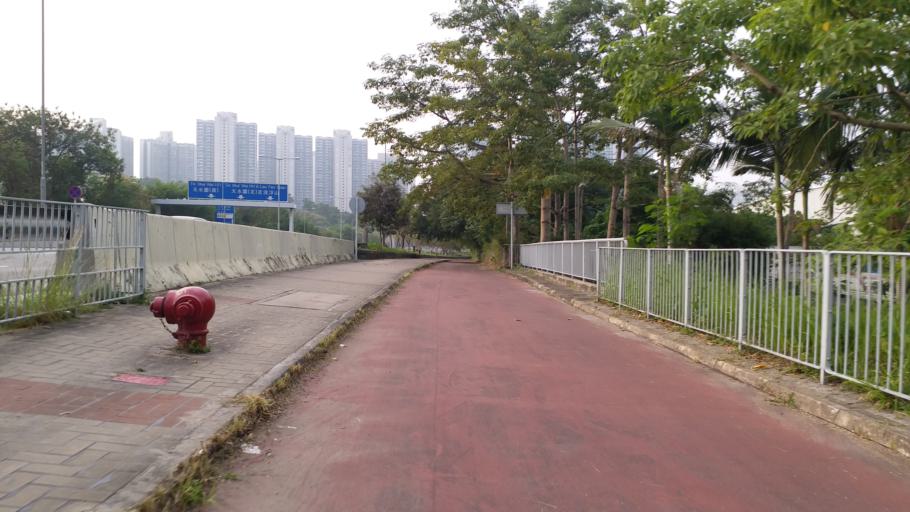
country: HK
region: Yuen Long
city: Yuen Long Kau Hui
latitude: 22.4481
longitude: 114.0116
